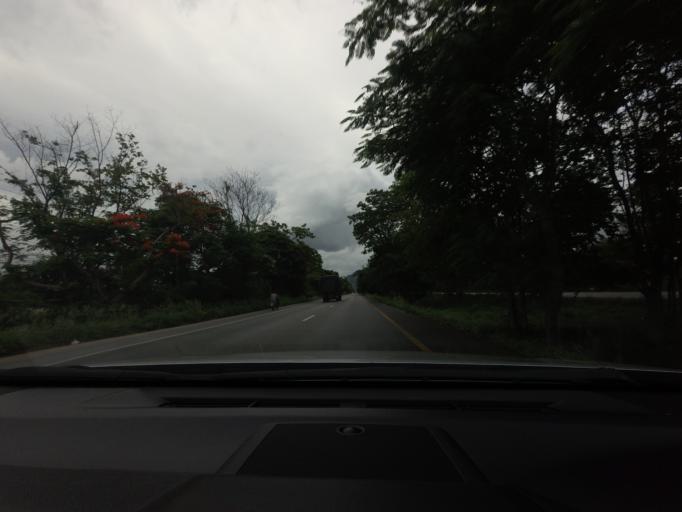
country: TH
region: Phetchaburi
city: Cha-am
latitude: 12.7823
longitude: 99.9379
